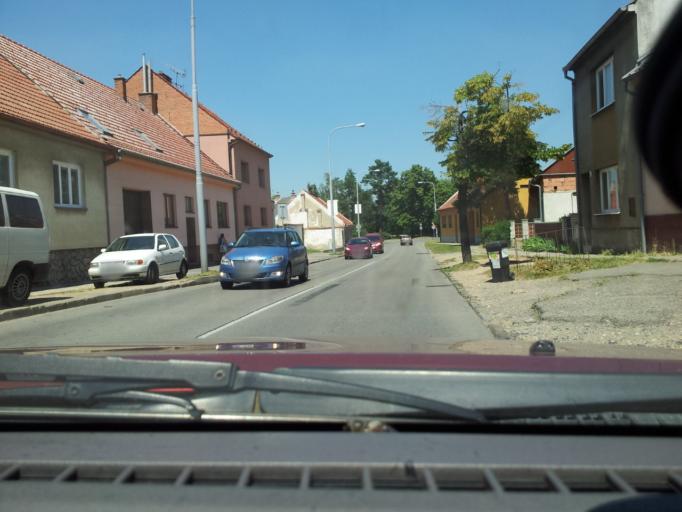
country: CZ
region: South Moravian
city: Rajhradice
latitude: 49.1440
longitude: 16.6651
